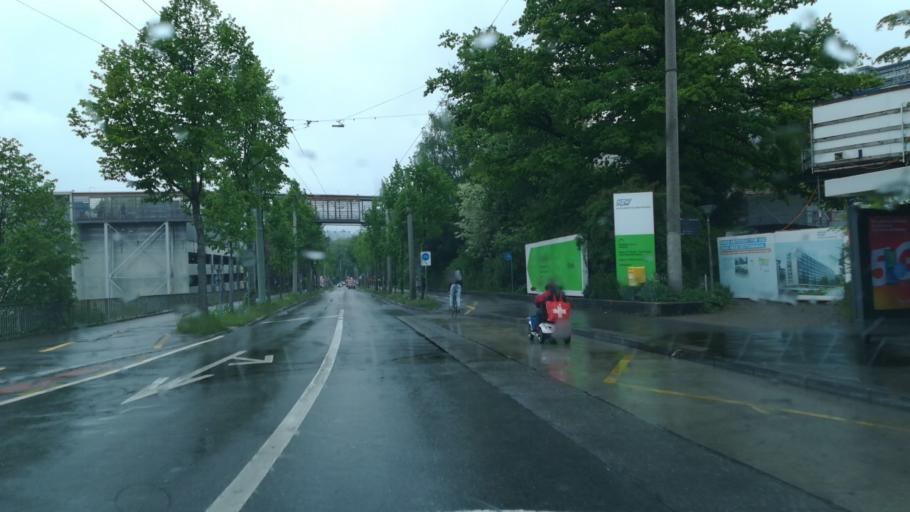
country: CH
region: Zurich
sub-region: Bezirk Winterthur
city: Stadt Winterthur (Kreis 1) / Lind
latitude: 47.5055
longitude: 8.7285
